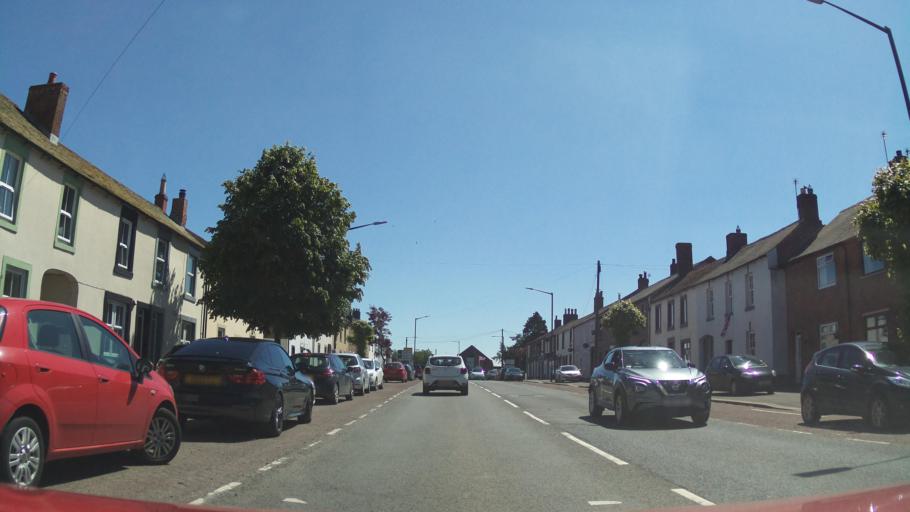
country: GB
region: Scotland
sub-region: Dumfries and Galloway
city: Gretna
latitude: 55.0080
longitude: -2.9715
